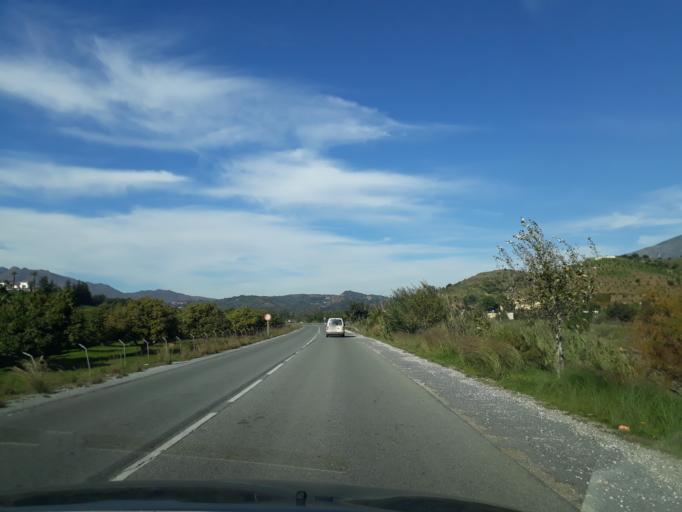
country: ES
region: Andalusia
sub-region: Provincia de Malaga
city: Fuengirola
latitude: 36.5449
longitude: -4.6882
